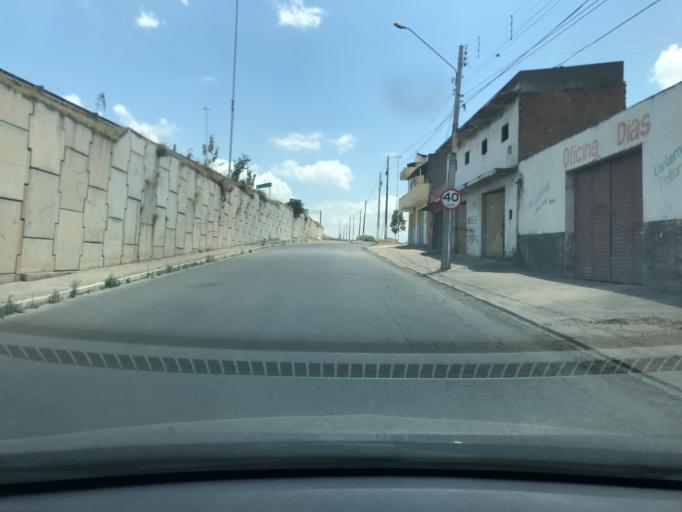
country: BR
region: Pernambuco
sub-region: Bezerros
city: Bezerros
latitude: -8.2466
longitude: -35.7578
